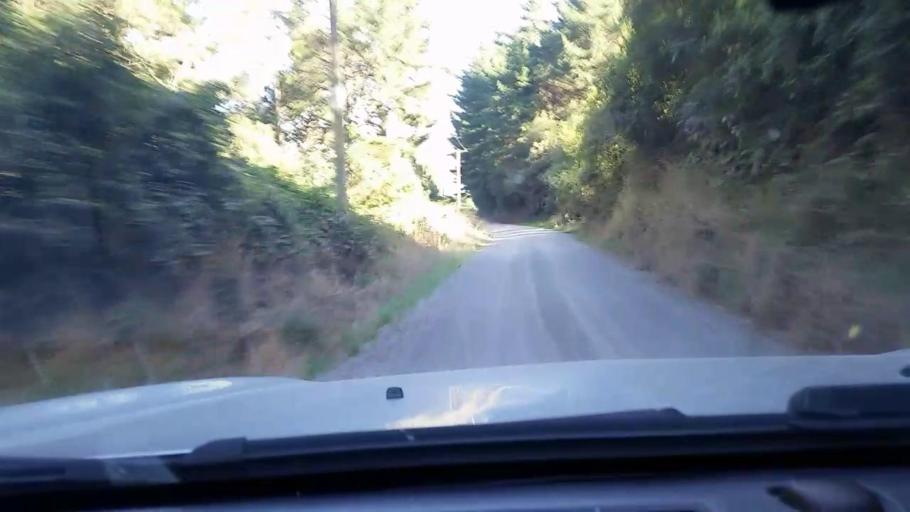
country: NZ
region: Bay of Plenty
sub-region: Rotorua District
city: Rotorua
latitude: -38.3901
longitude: 176.1708
